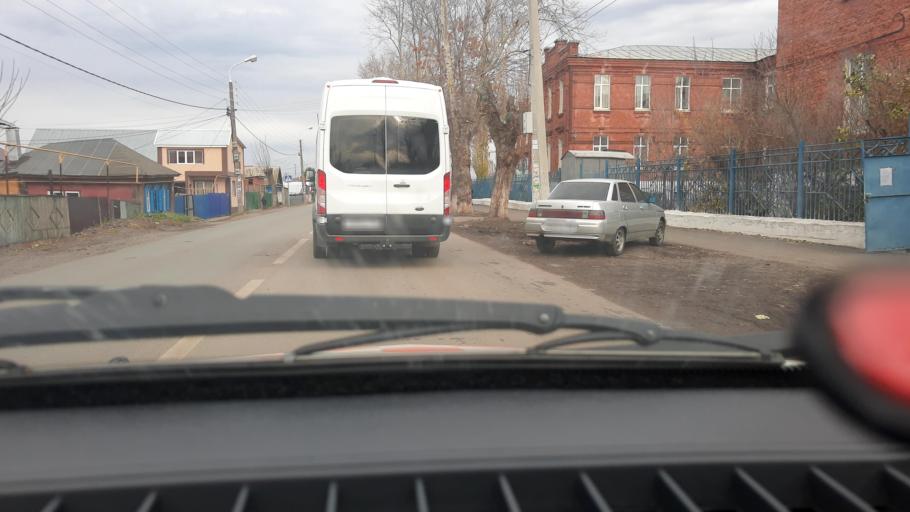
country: RU
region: Bashkortostan
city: Ufa
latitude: 54.7325
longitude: 55.9159
